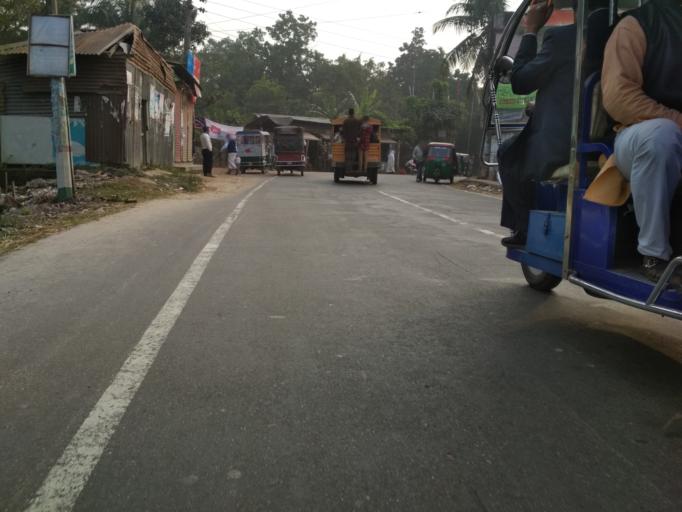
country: BD
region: Chittagong
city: Lakshmipur
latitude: 22.9374
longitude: 90.8415
